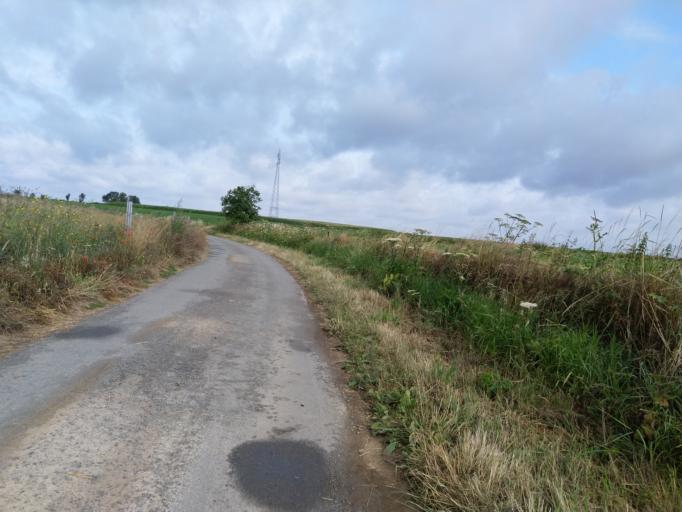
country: BE
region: Wallonia
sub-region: Province du Hainaut
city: Lens
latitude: 50.5524
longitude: 3.8750
